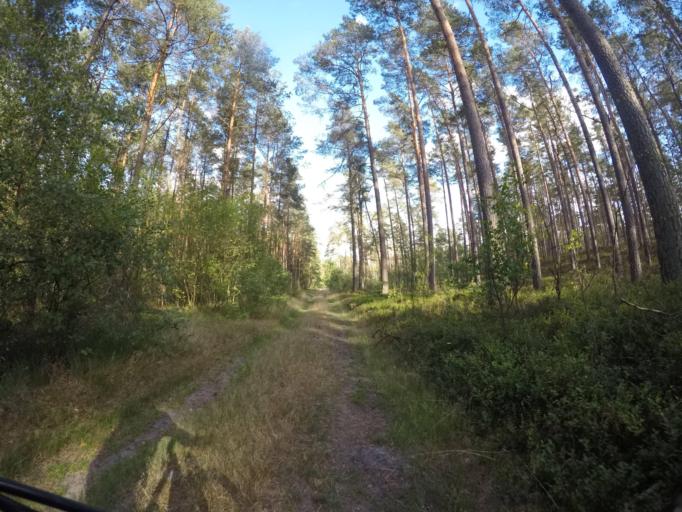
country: DE
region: Mecklenburg-Vorpommern
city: Lubtheen
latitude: 53.2445
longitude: 11.0141
